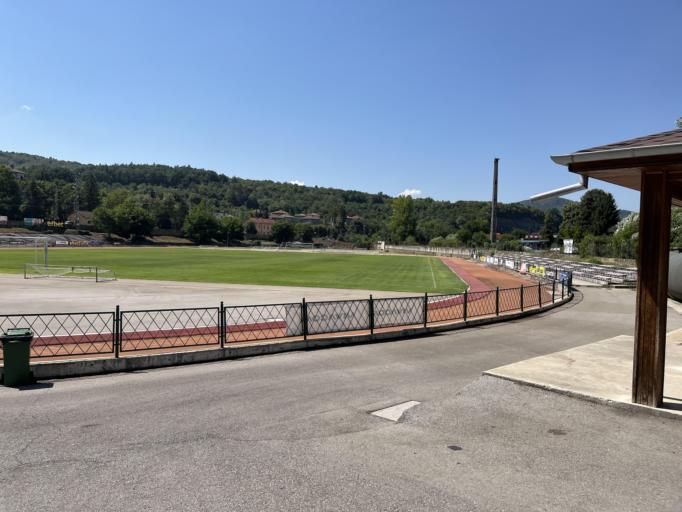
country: BG
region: Gabrovo
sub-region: Obshtina Dryanovo
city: Dryanovo
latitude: 42.9738
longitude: 25.4774
